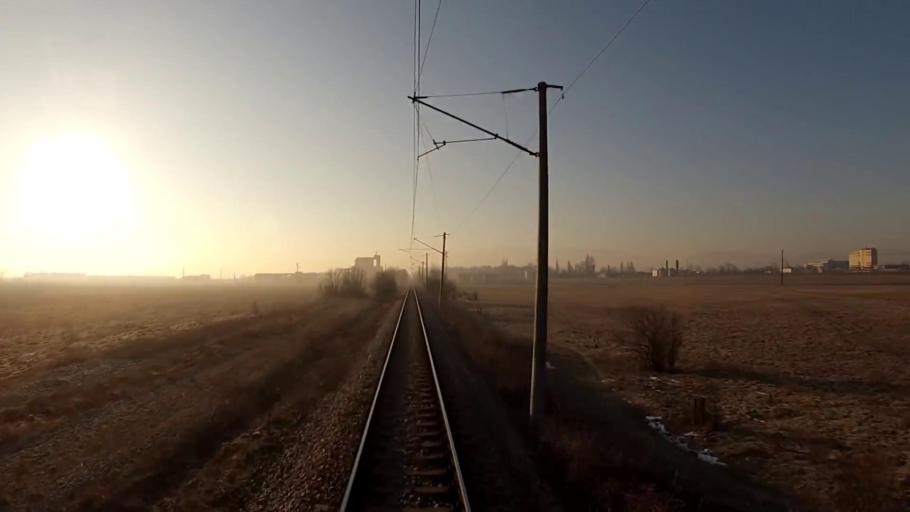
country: BG
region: Sofiya
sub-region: Obshtina Kostinbrod
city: Kostinbrod
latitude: 42.7933
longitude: 23.2090
